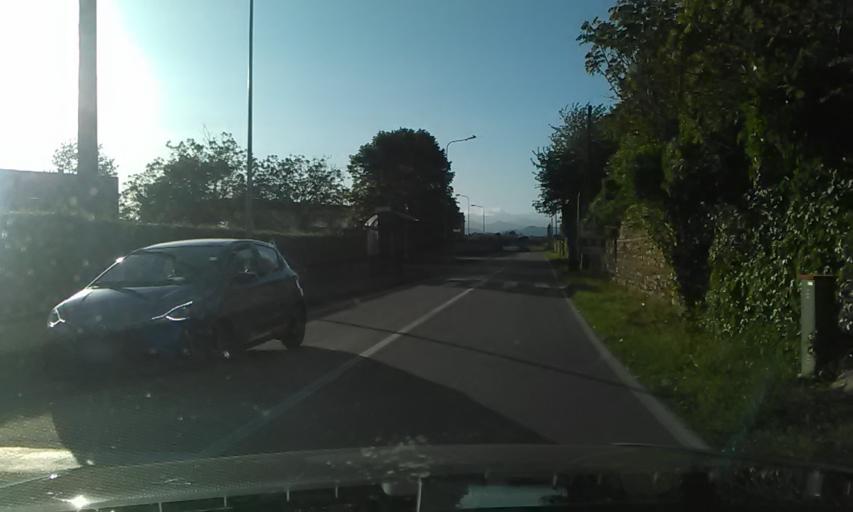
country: IT
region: Piedmont
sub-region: Provincia di Novara
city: Momo
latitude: 45.5679
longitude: 8.5399
